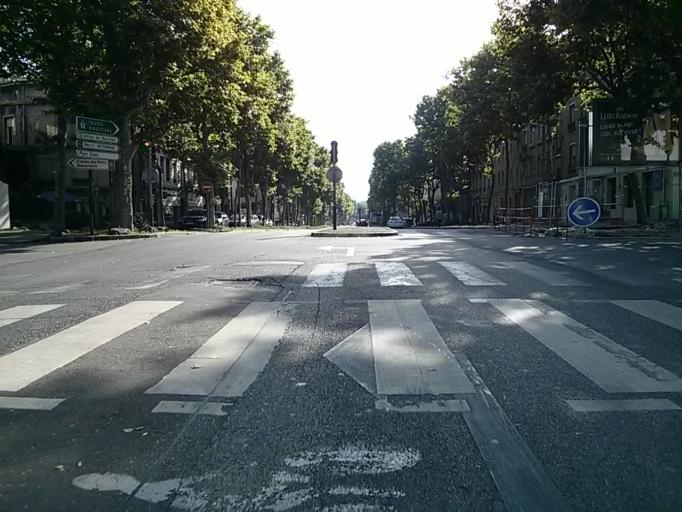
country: FR
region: Rhone-Alpes
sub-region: Departement de la Loire
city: Saint-Etienne
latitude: 45.4473
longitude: 4.3861
